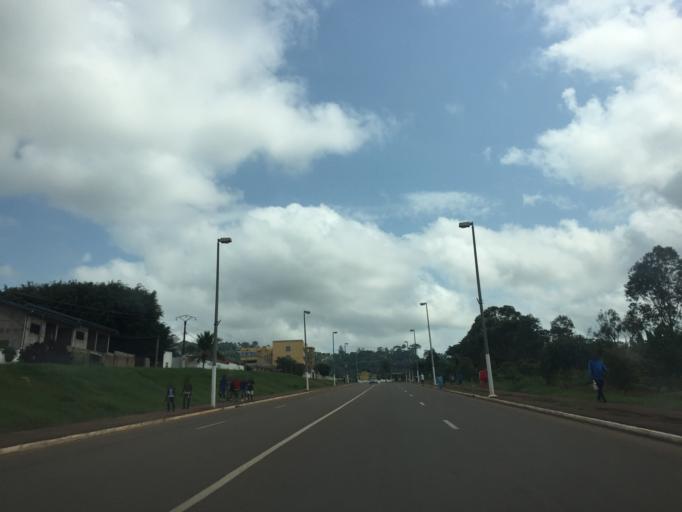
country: CM
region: Centre
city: Yaounde
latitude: 3.9031
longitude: 11.5040
